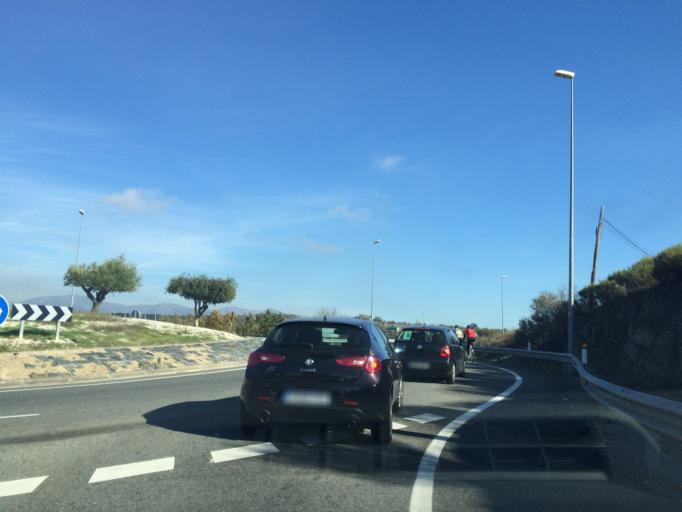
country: ES
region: Madrid
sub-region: Provincia de Madrid
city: Miraflores de la Sierra
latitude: 40.7590
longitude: -3.7645
